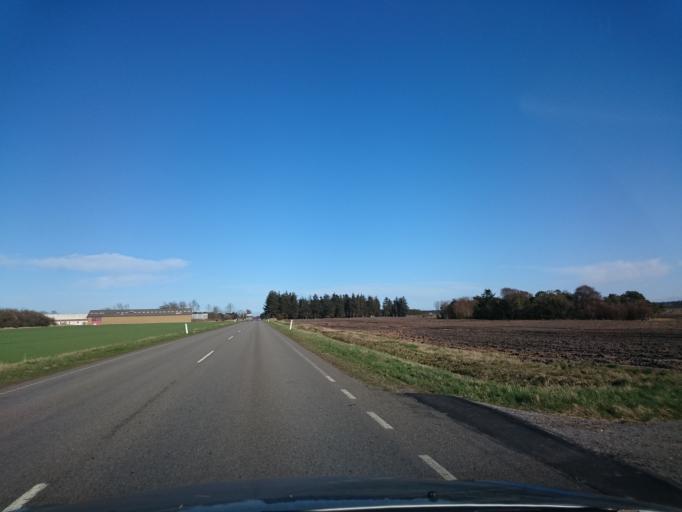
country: DK
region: North Denmark
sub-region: Frederikshavn Kommune
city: Strandby
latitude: 57.6060
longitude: 10.3413
